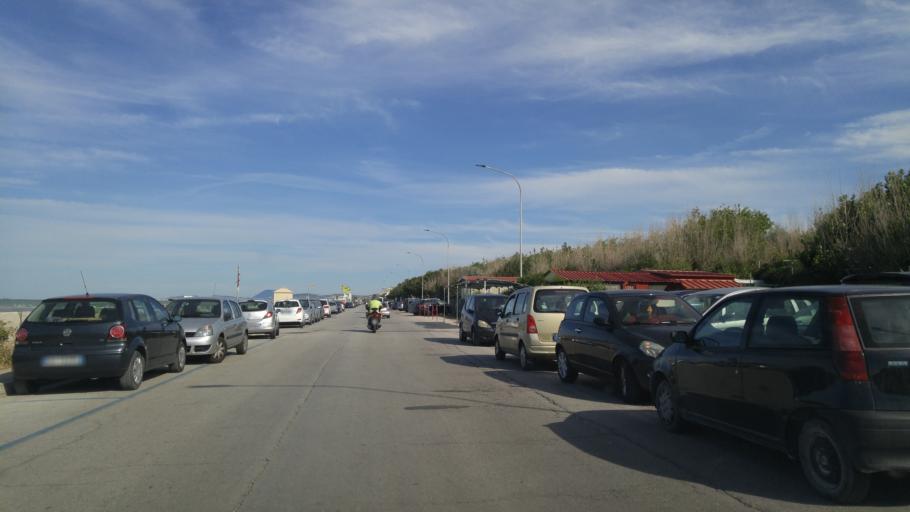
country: IT
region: The Marches
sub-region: Provincia di Ancona
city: Montignano-Marzocca
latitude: 43.6886
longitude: 13.2678
